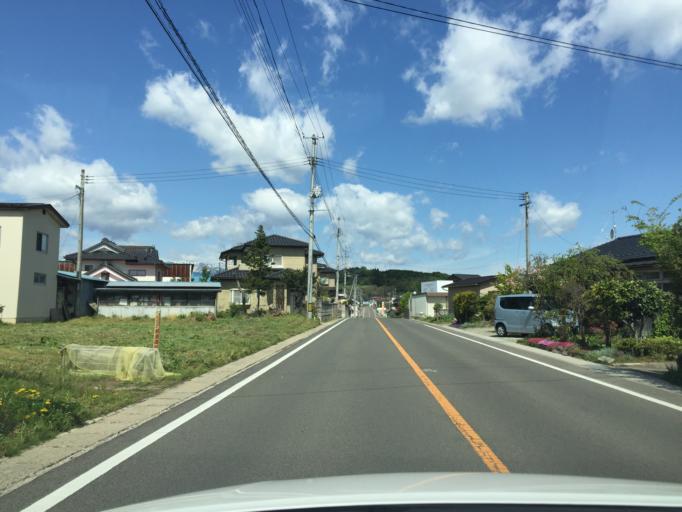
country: JP
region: Fukushima
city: Nihommatsu
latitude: 37.6565
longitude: 140.4714
